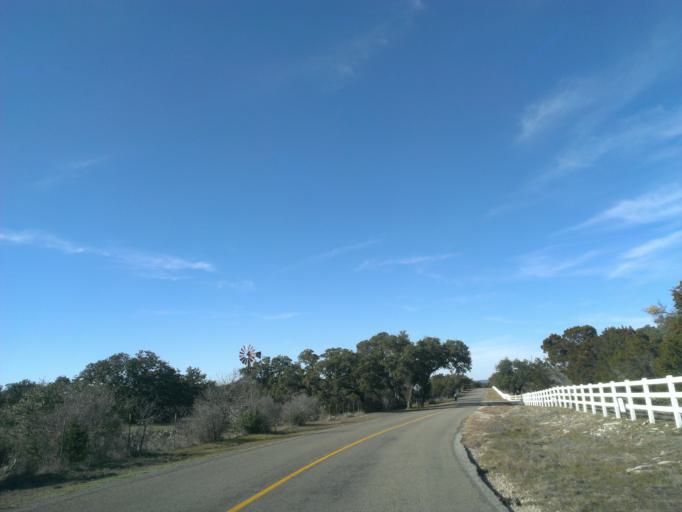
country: US
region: Texas
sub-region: Burnet County
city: Meadowlakes
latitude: 30.5291
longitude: -98.2680
